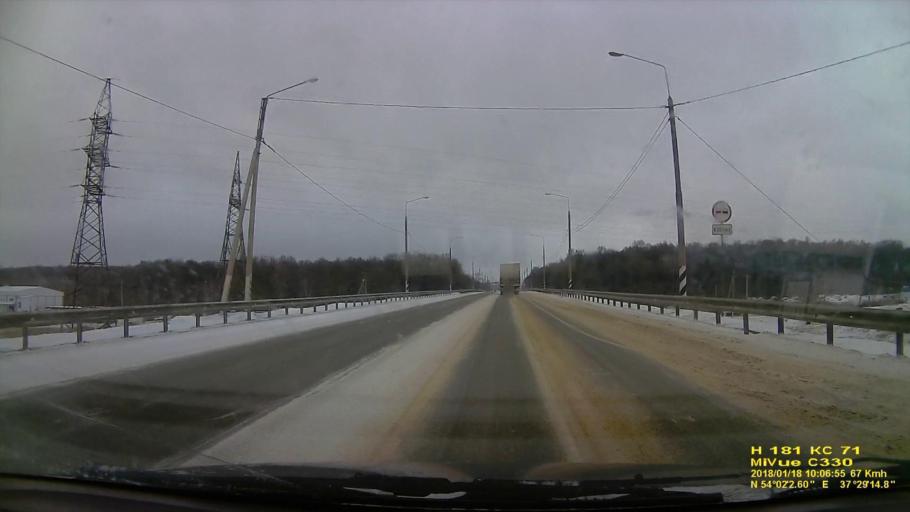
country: RU
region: Tula
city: Pervomayskiy
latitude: 54.0335
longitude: 37.4875
